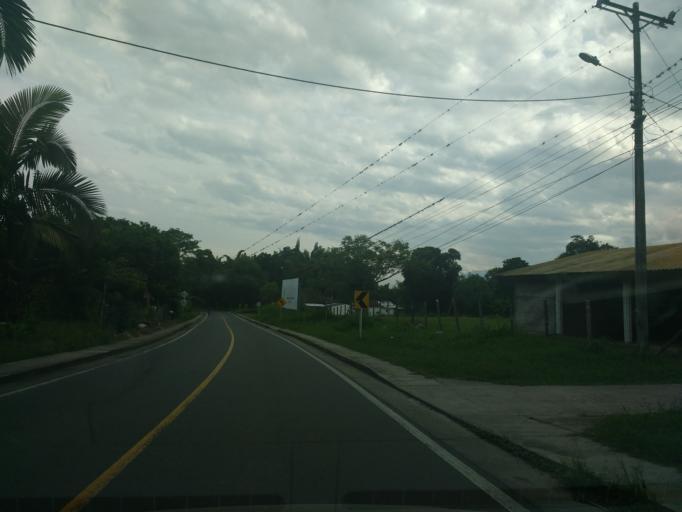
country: CO
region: Cauca
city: Miranda
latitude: 3.2775
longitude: -76.2214
